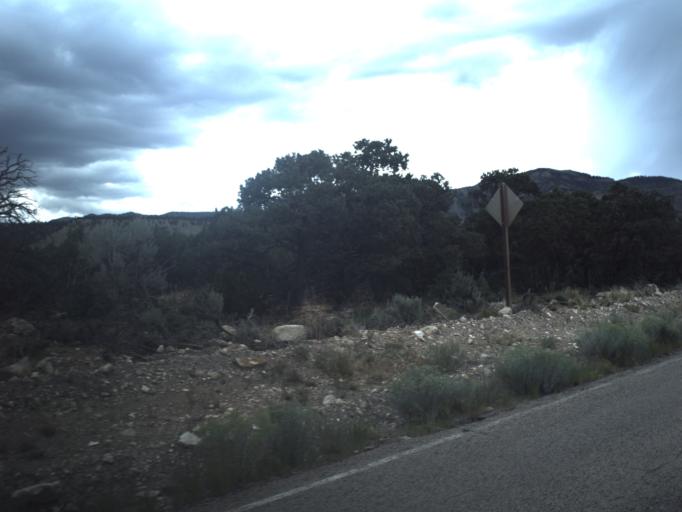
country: US
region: Utah
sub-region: Emery County
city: Huntington
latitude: 39.4841
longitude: -110.9674
